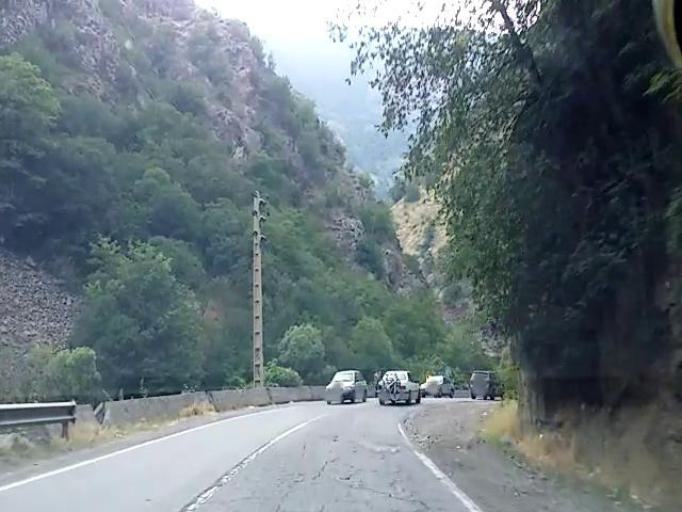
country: IR
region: Mazandaran
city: Chalus
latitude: 36.2873
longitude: 51.2424
